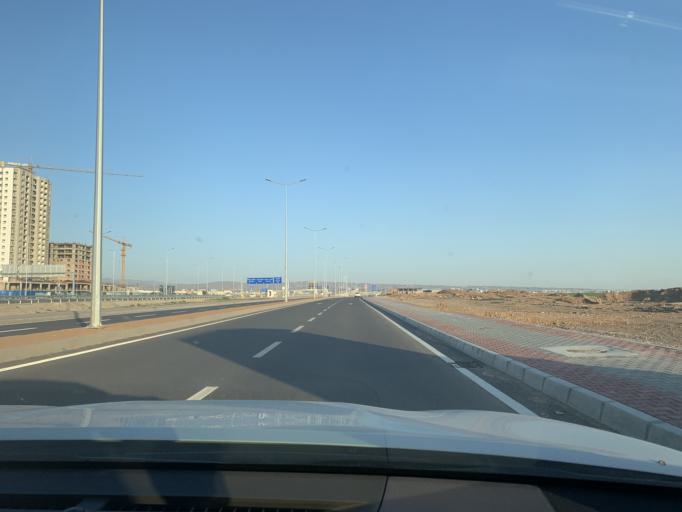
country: IQ
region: Arbil
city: Erbil
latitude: 36.2870
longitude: 44.0381
